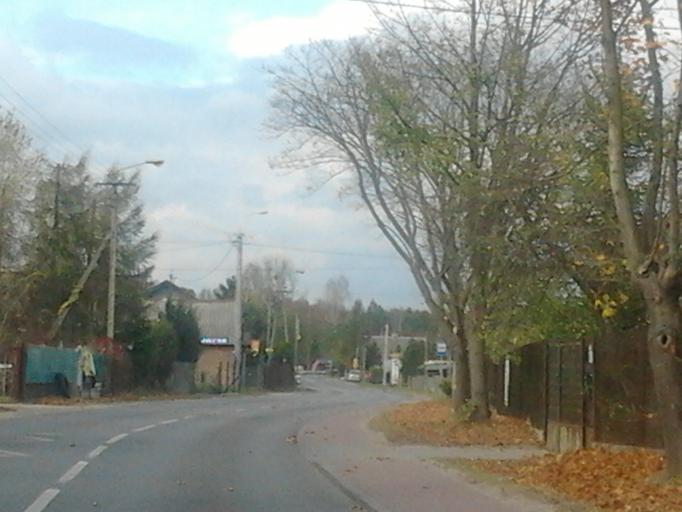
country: PL
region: Masovian Voivodeship
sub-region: Powiat pruszkowski
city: Granica
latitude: 52.1154
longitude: 20.7977
